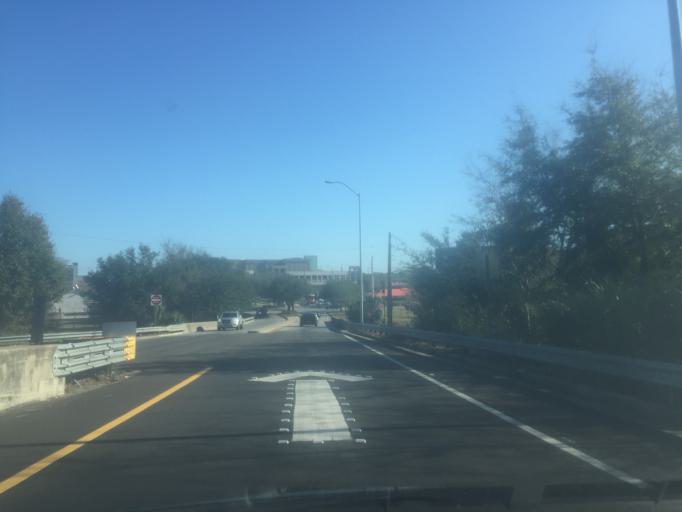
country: US
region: Georgia
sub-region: Chatham County
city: Savannah
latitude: 32.0805
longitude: -81.1039
